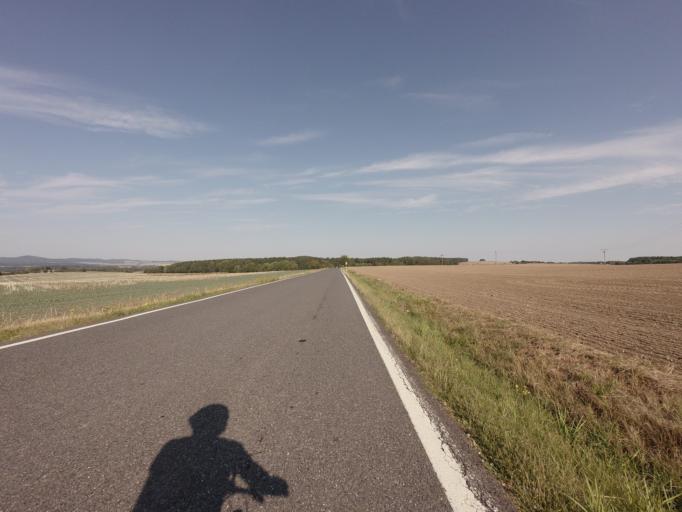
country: CZ
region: Jihocesky
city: Bernartice
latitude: 49.3091
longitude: 14.3767
